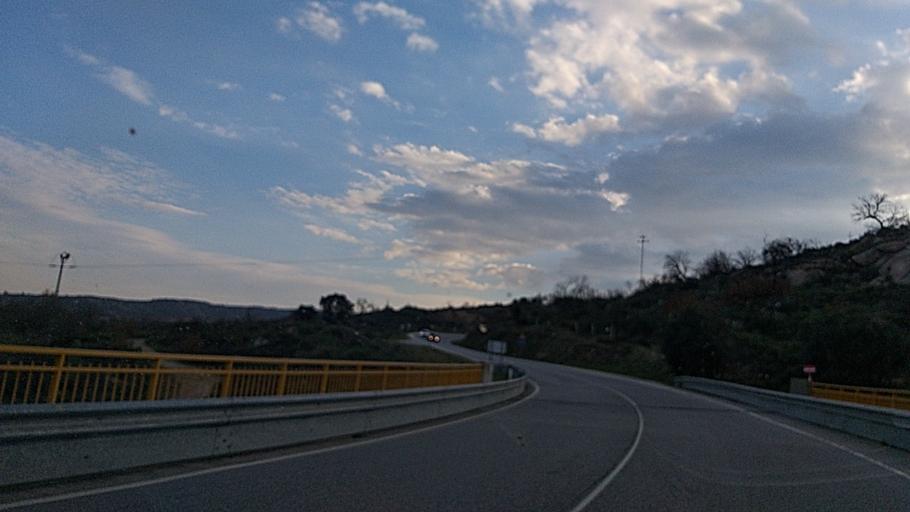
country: ES
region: Castille and Leon
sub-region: Provincia de Salamanca
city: Aldea del Obispo
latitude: 40.7028
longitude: -6.9323
